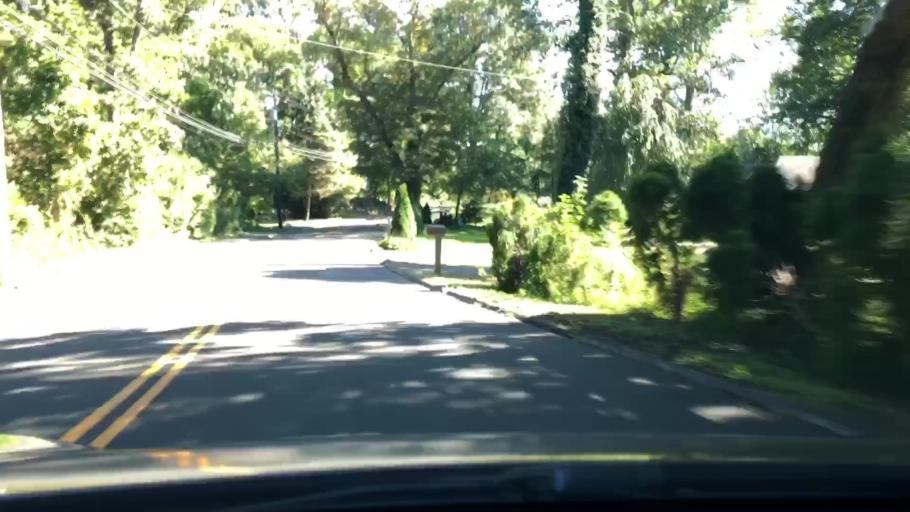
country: US
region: Connecticut
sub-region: Fairfield County
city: Darien
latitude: 41.1076
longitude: -73.4446
